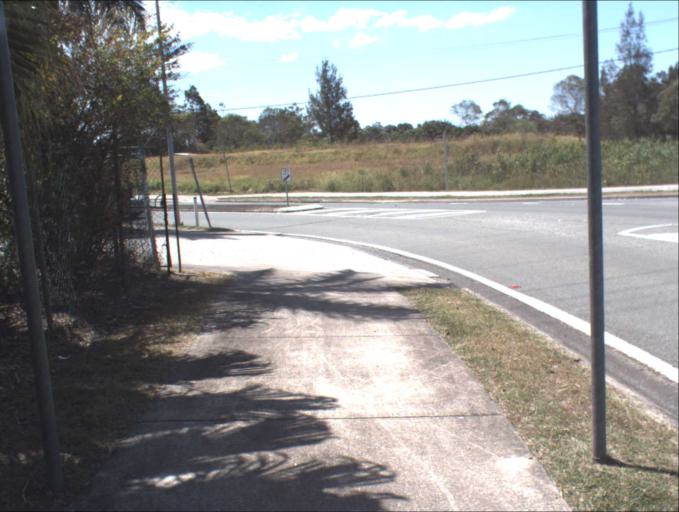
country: AU
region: Queensland
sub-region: Gold Coast
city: Yatala
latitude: -27.7221
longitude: 153.2178
